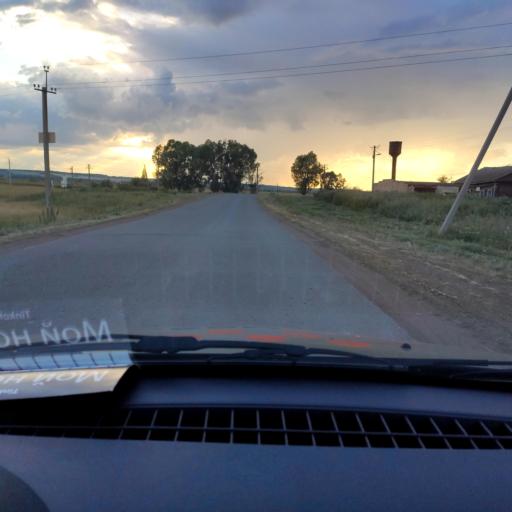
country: RU
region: Bashkortostan
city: Mikhaylovka
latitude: 54.9717
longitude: 55.7874
